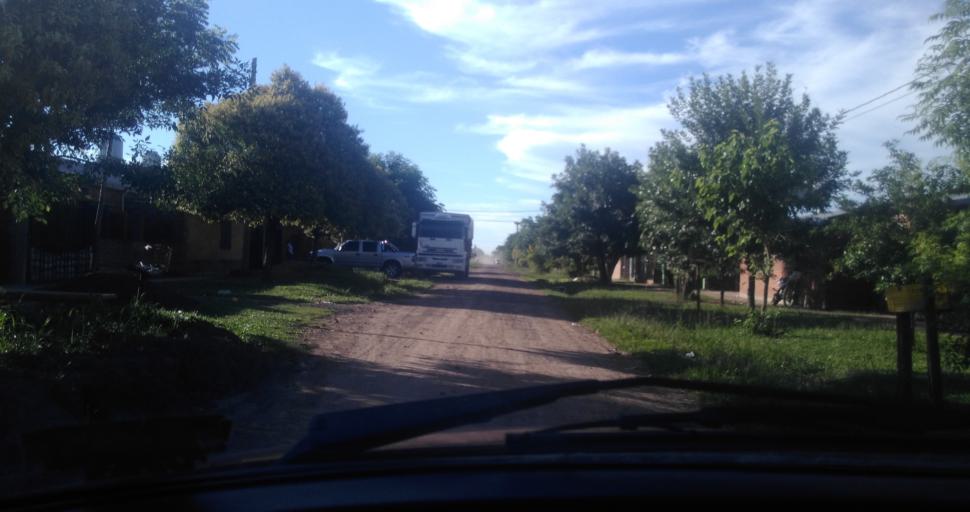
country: AR
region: Chaco
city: Fontana
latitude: -27.4145
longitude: -59.0240
